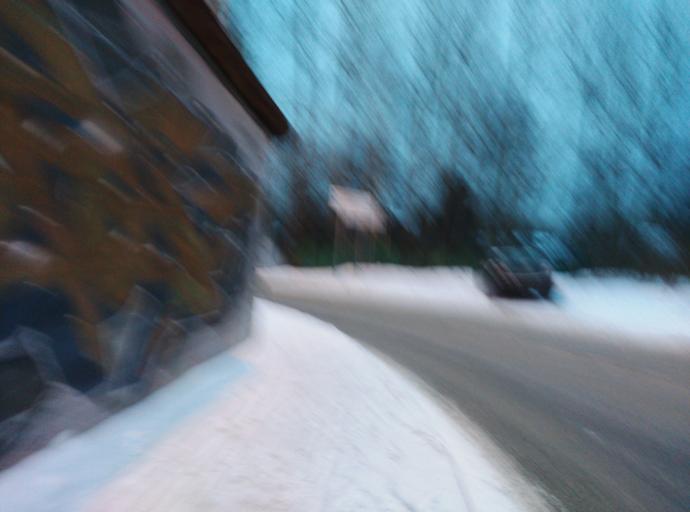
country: RU
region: St.-Petersburg
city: Kolomyagi
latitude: 60.0227
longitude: 30.2977
